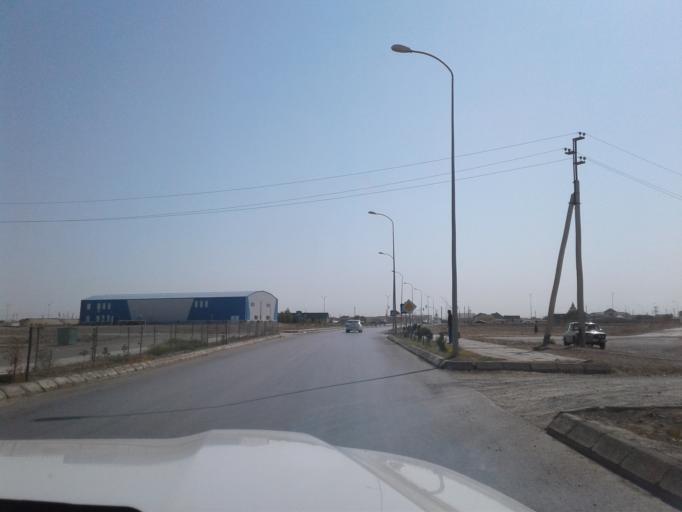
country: TM
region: Balkan
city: Gazanjyk
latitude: 39.2480
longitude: 55.5296
